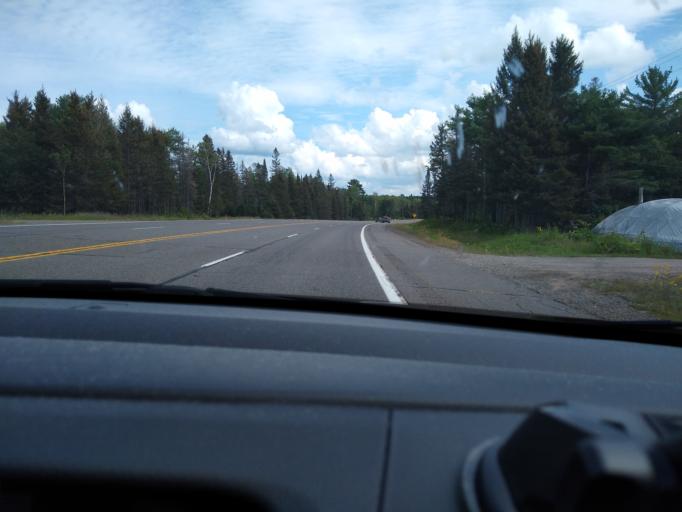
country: US
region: Michigan
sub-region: Marquette County
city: West Ishpeming
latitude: 46.5354
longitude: -88.0133
